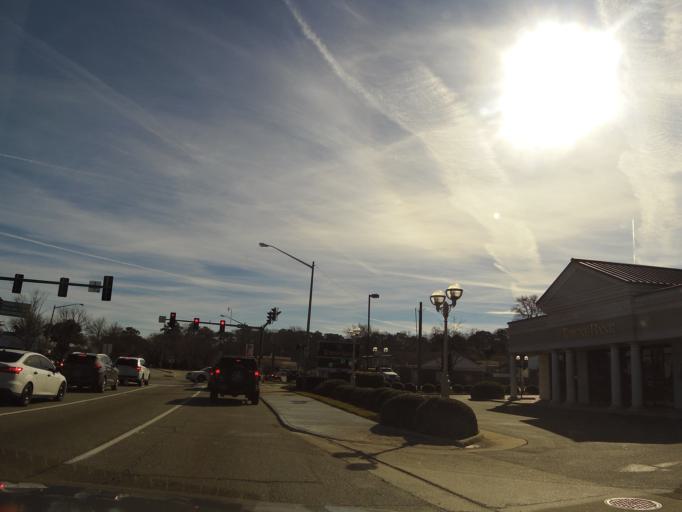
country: US
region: Virginia
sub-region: City of Newport News
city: Newport News
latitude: 37.0435
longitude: -76.4733
